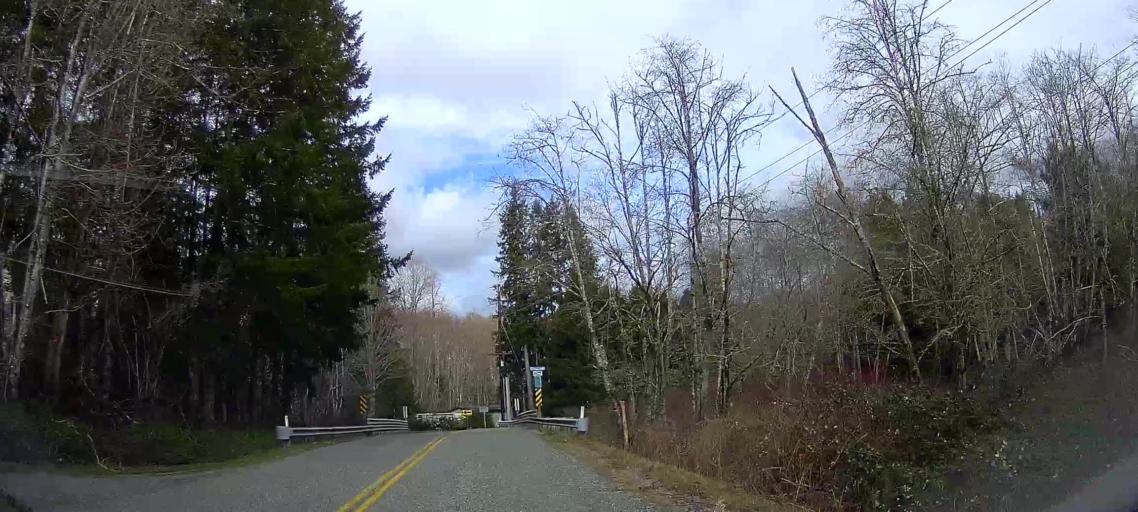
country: US
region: Washington
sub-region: Skagit County
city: Burlington
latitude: 48.5964
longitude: -122.3282
